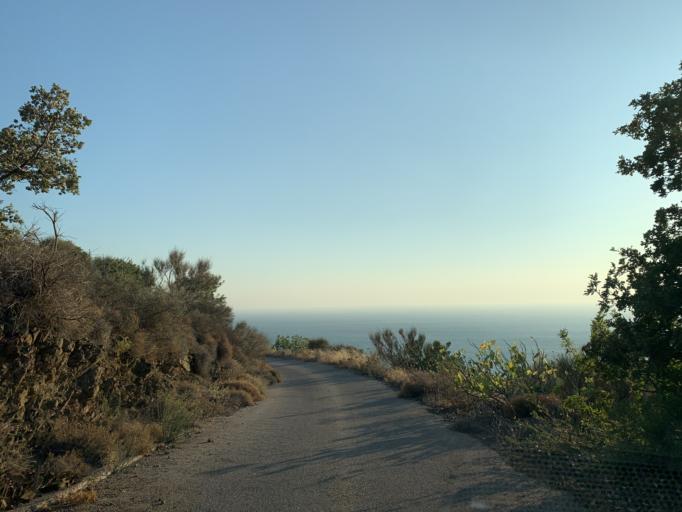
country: GR
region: North Aegean
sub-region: Chios
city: Psara
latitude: 38.5251
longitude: 25.8525
